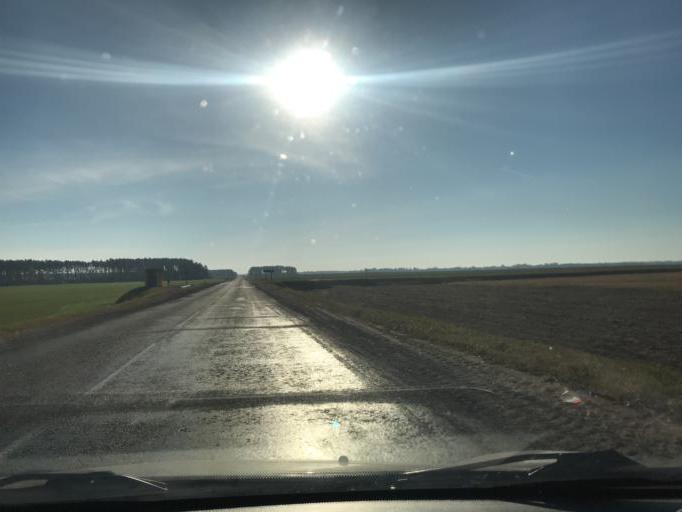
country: BY
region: Gomel
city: Khoyniki
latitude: 51.8214
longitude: 30.0794
